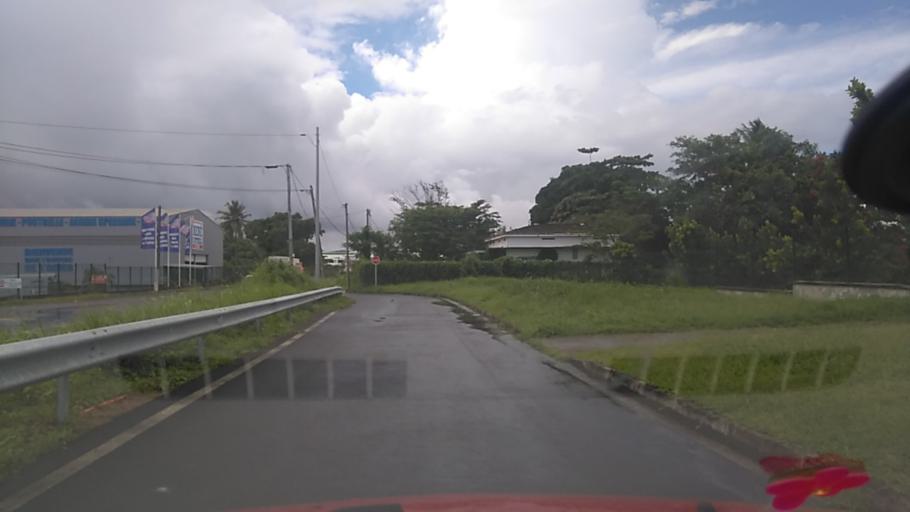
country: MQ
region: Martinique
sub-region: Martinique
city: Le Lamentin
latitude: 14.6283
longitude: -60.9894
